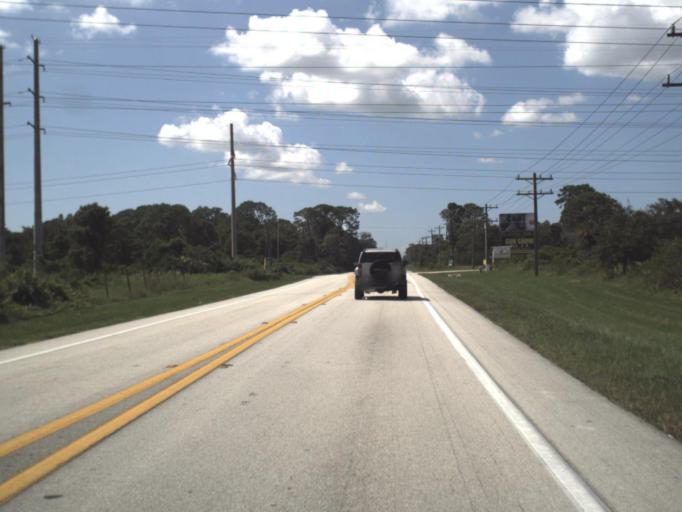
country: US
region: Florida
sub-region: Lee County
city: Fort Myers Shores
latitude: 26.7149
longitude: -81.7760
